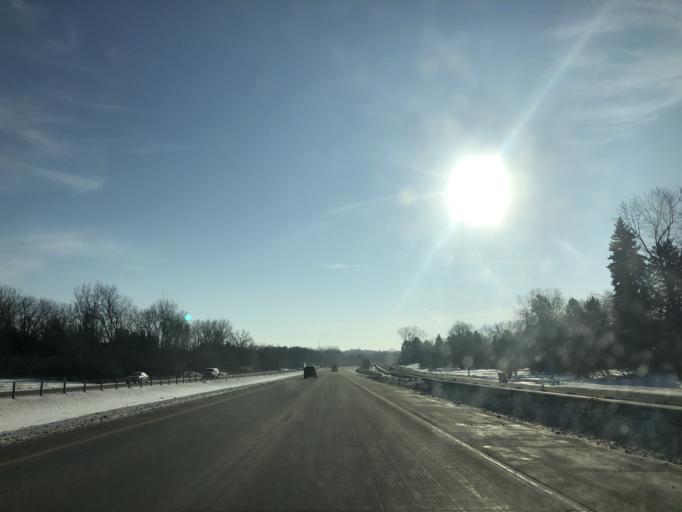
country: US
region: Minnesota
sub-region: Ramsey County
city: Shoreview
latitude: 45.0774
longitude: -93.1743
